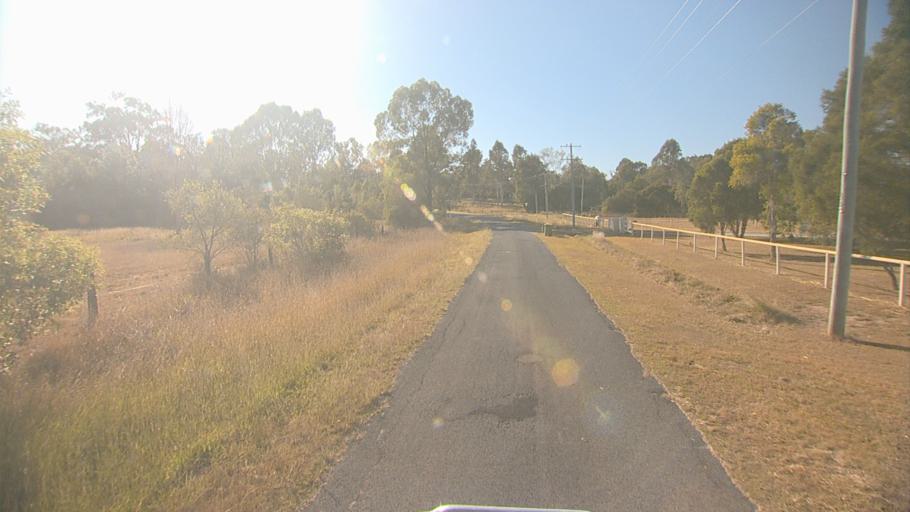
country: AU
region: Queensland
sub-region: Logan
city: Cedar Vale
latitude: -27.8395
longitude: 152.9943
